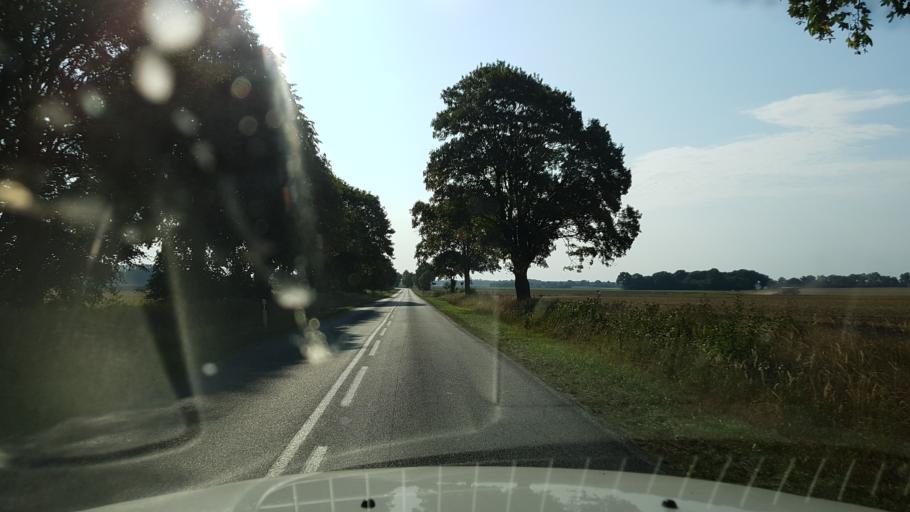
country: PL
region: West Pomeranian Voivodeship
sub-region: Powiat gryficki
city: Ploty
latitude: 53.7951
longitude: 15.2807
